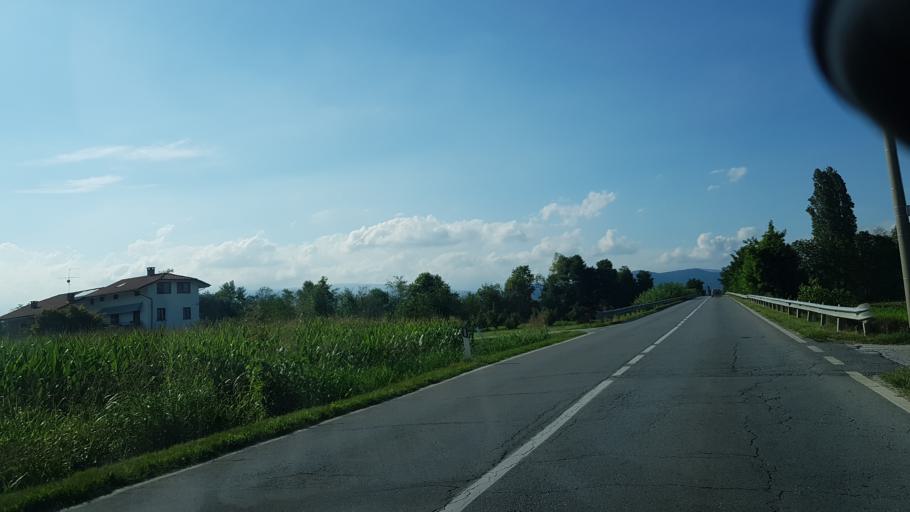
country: IT
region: Piedmont
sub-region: Provincia di Cuneo
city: Roata Rossi
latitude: 44.4523
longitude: 7.5243
